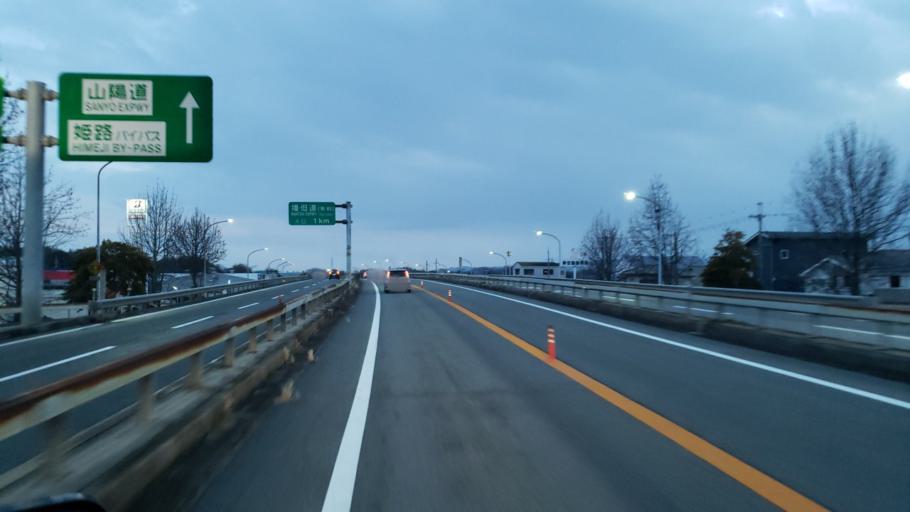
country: JP
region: Hyogo
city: Himeji
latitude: 34.9435
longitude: 134.7615
